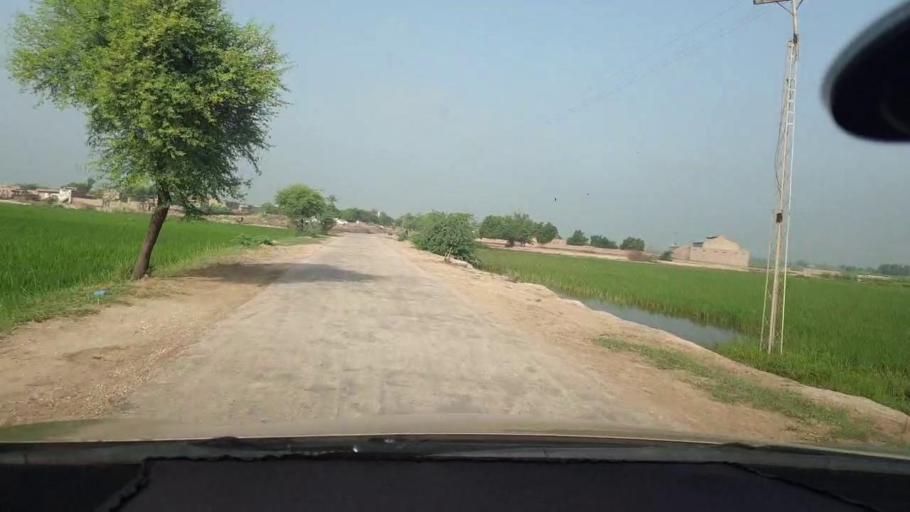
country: PK
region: Sindh
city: Goth Garelo
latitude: 27.4777
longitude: 68.0107
